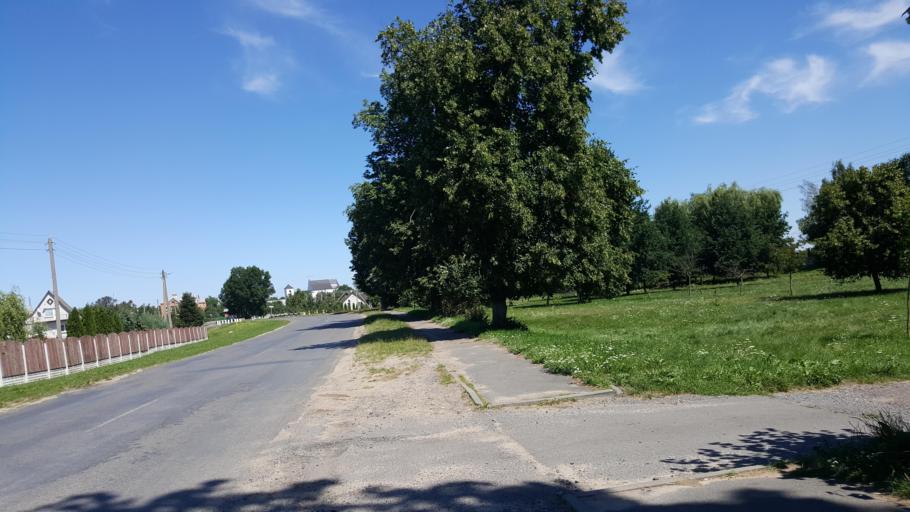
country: BY
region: Brest
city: Charnawchytsy
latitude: 52.2125
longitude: 23.7387
